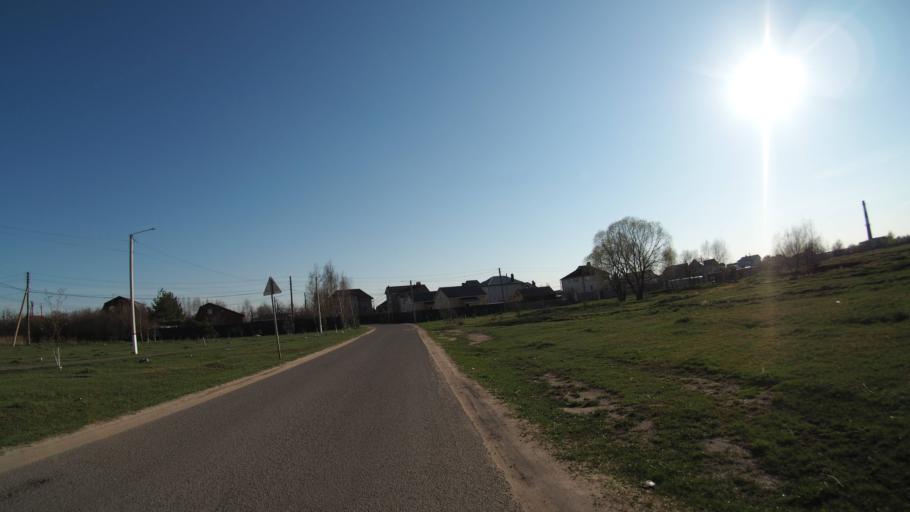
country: RU
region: Moskovskaya
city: Malyshevo
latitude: 55.5049
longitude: 38.3362
